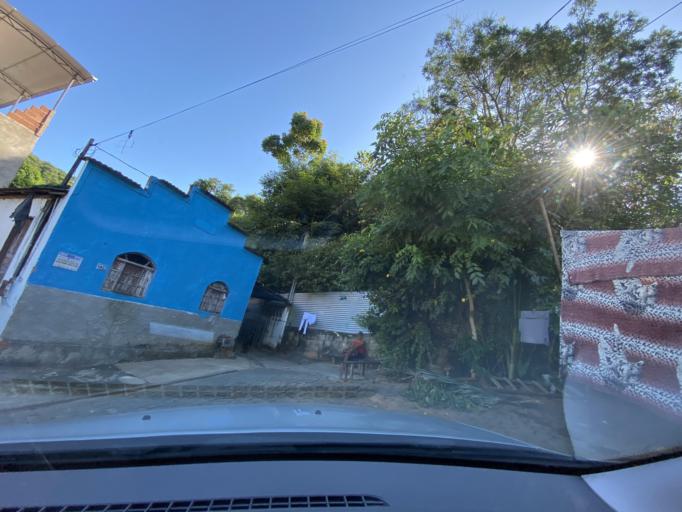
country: BR
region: Espirito Santo
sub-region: Jeronimo Monteiro
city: Jeronimo Monteiro
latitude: -20.7918
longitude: -41.3979
